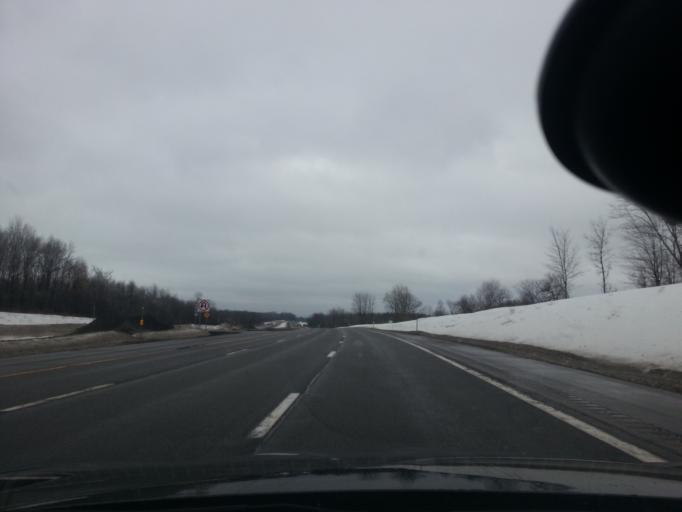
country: US
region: New York
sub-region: Oswego County
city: Central Square
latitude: 43.2694
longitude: -76.1314
